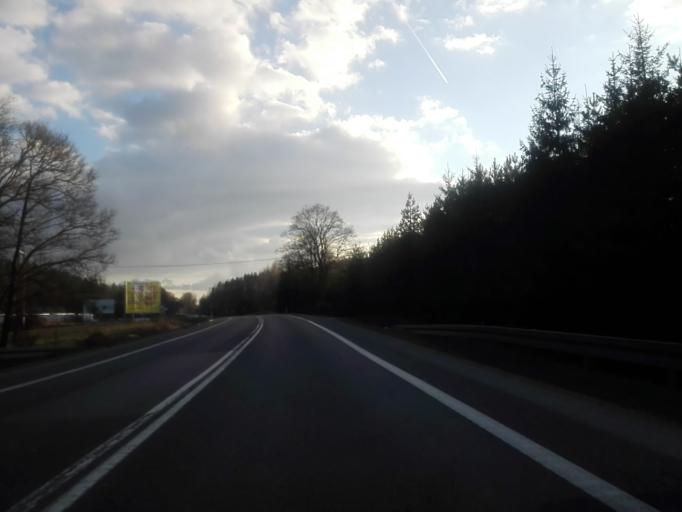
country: PL
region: Podlasie
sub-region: Suwalki
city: Suwalki
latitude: 54.1457
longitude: 22.9659
